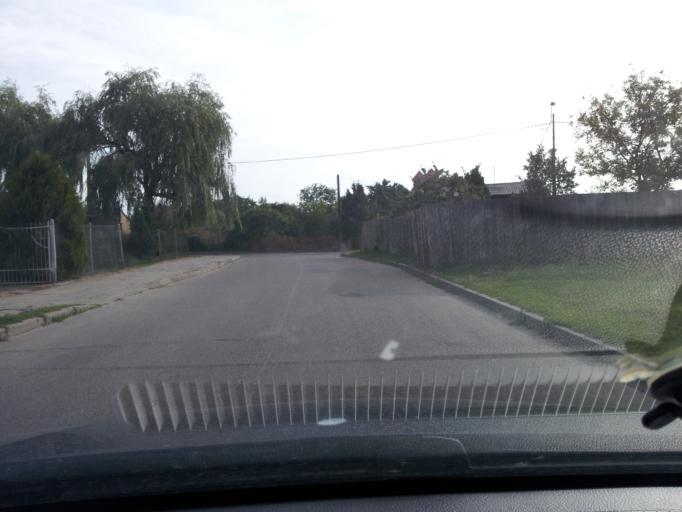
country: PL
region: Kujawsko-Pomorskie
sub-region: Powiat brodnicki
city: Gorzno
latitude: 53.1964
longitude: 19.6428
